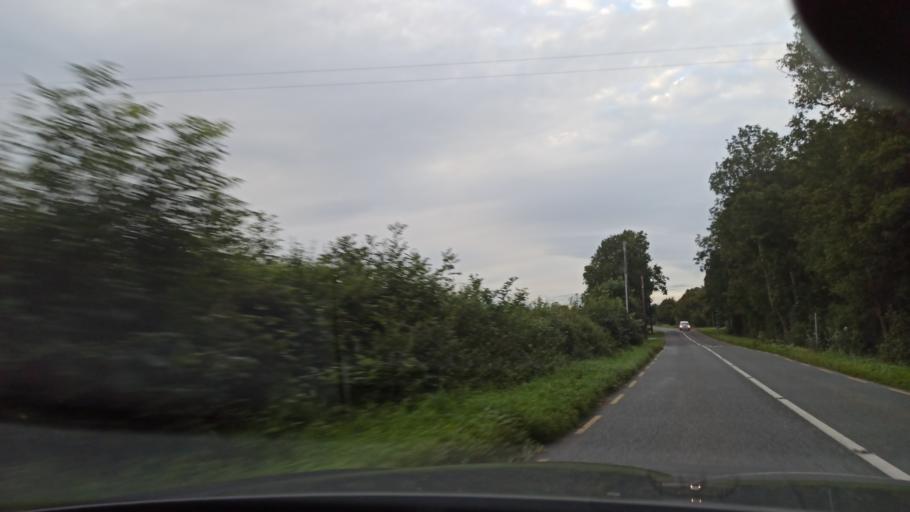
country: IE
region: Munster
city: Cashel
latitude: 52.4885
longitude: -7.8575
